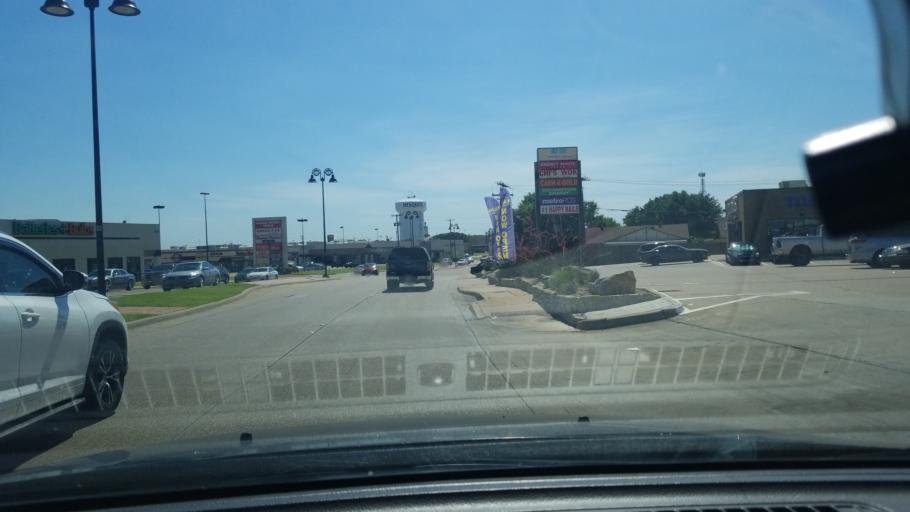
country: US
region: Texas
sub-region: Dallas County
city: Mesquite
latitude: 32.8112
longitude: -96.6116
